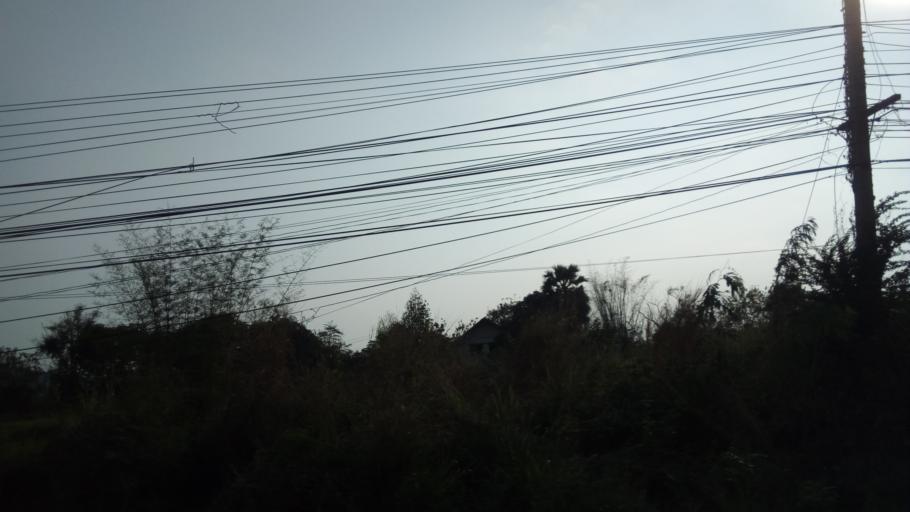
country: TH
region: Sara Buri
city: Saraburi
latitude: 14.4585
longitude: 100.9454
